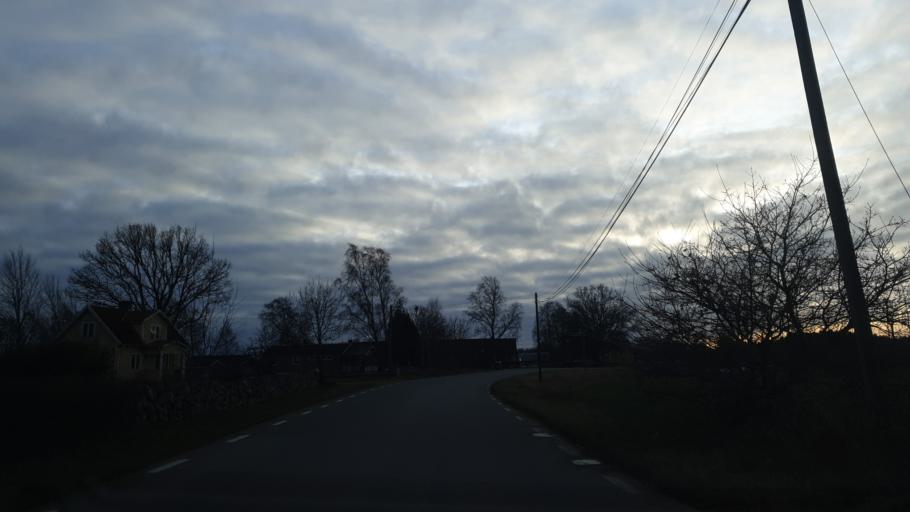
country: SE
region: Blekinge
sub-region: Karlskrona Kommun
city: Jaemjoe
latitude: 56.1851
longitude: 15.9420
